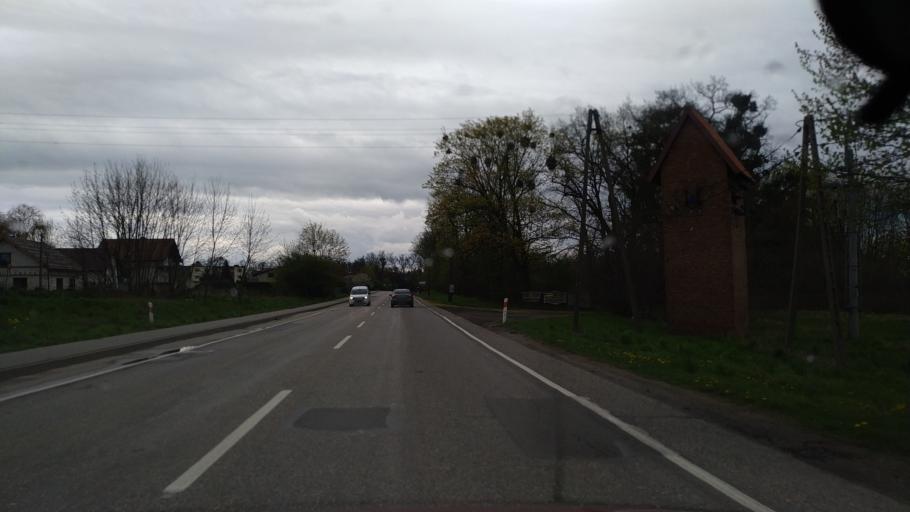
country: PL
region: Pomeranian Voivodeship
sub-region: Powiat tczewski
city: Pelplin
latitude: 54.0349
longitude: 18.6560
